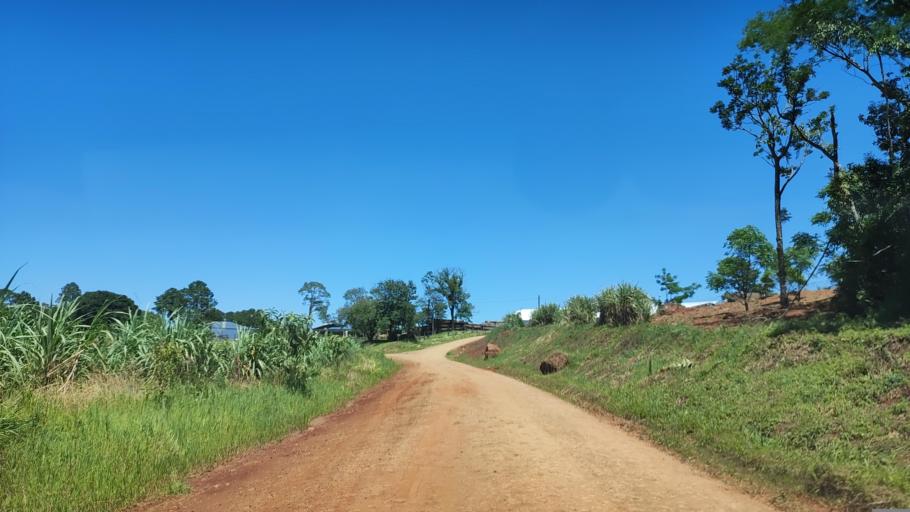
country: AR
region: Misiones
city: Dos de Mayo
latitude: -27.0114
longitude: -54.6184
